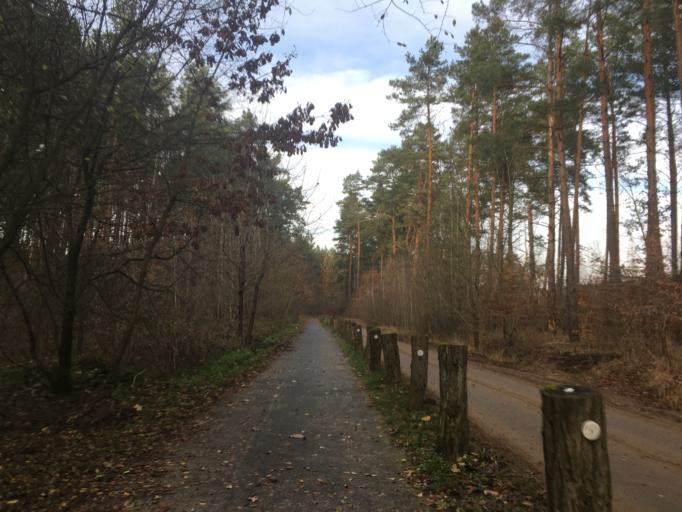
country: DE
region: Brandenburg
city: Niederfinow
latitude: 52.8489
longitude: 13.9024
